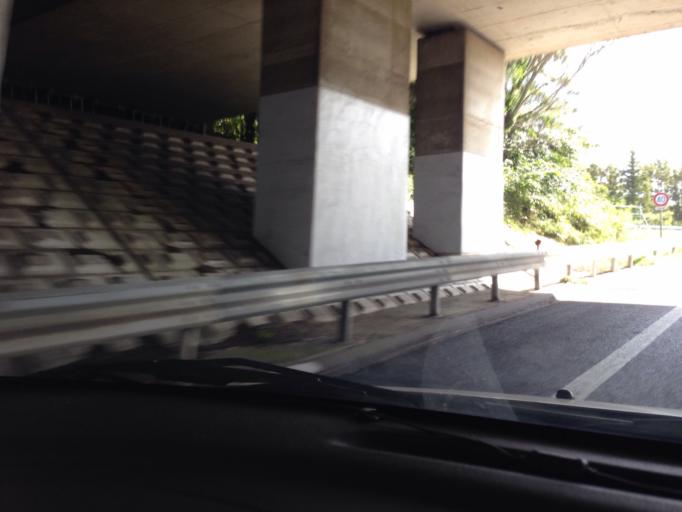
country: JP
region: Ibaraki
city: Naka
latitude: 36.0602
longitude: 140.1576
